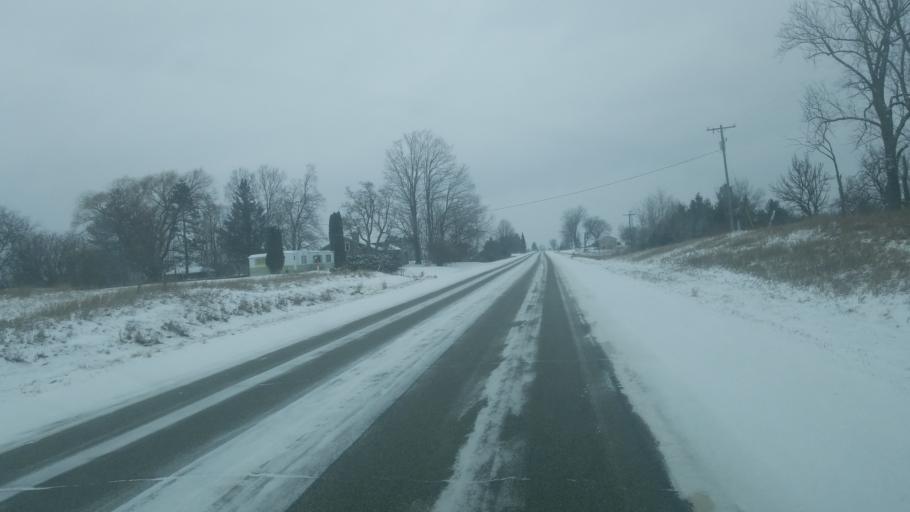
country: US
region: Michigan
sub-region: Osceola County
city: Evart
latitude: 43.9058
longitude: -85.1478
